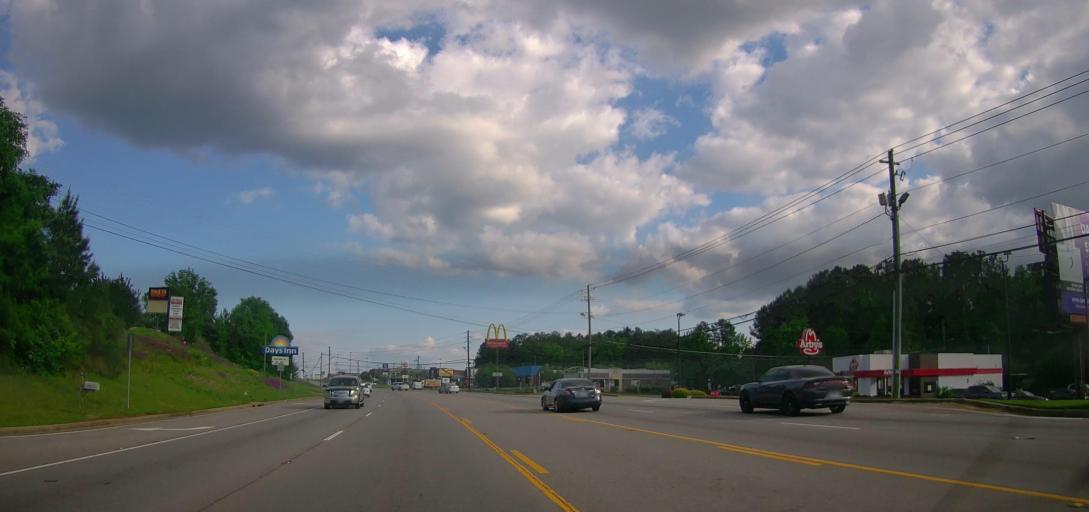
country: US
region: Georgia
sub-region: Baldwin County
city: Milledgeville
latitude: 33.1144
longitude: -83.2597
